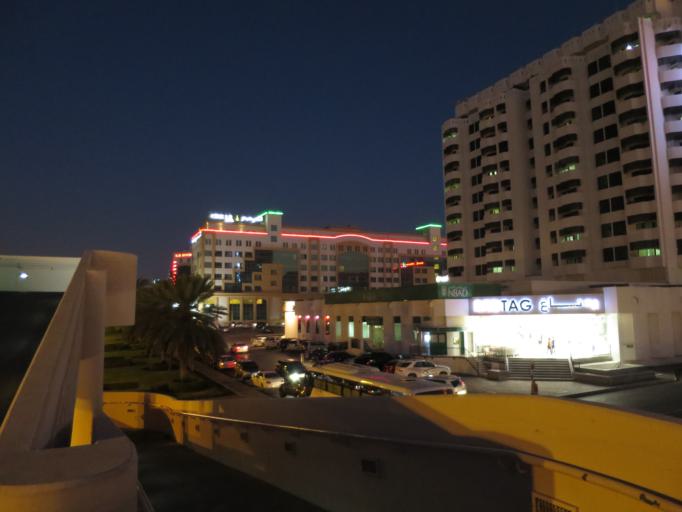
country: OM
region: Muhafazat Masqat
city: Bawshar
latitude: 23.5969
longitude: 58.4226
